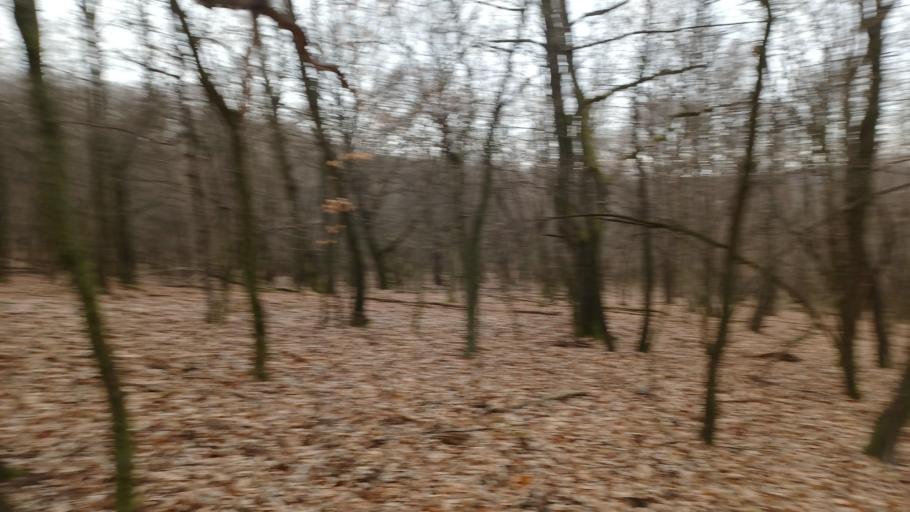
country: HU
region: Tolna
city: Szentgalpuszta
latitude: 46.2973
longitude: 18.6262
